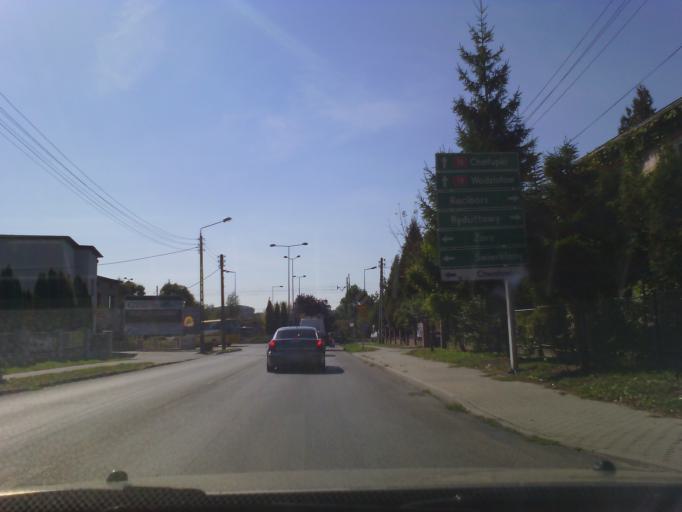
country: PL
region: Silesian Voivodeship
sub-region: Rybnik
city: Rybnik
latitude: 50.0861
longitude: 18.5299
